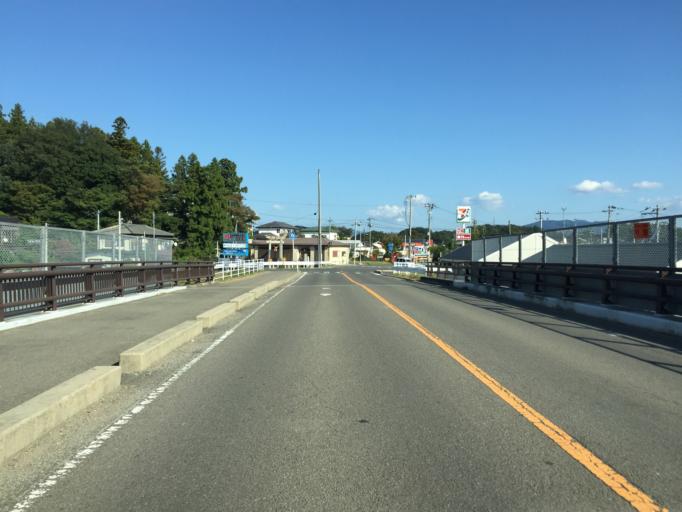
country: JP
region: Fukushima
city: Nihommatsu
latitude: 37.6550
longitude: 140.4839
